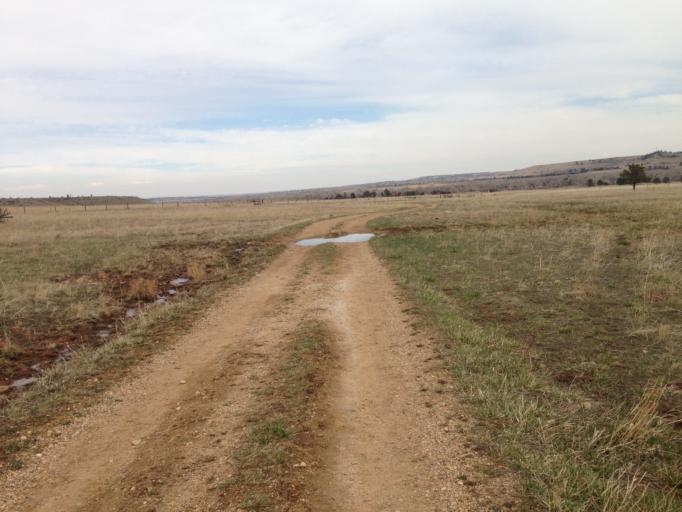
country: US
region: Colorado
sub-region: Boulder County
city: Boulder
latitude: 39.9562
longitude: -105.2538
